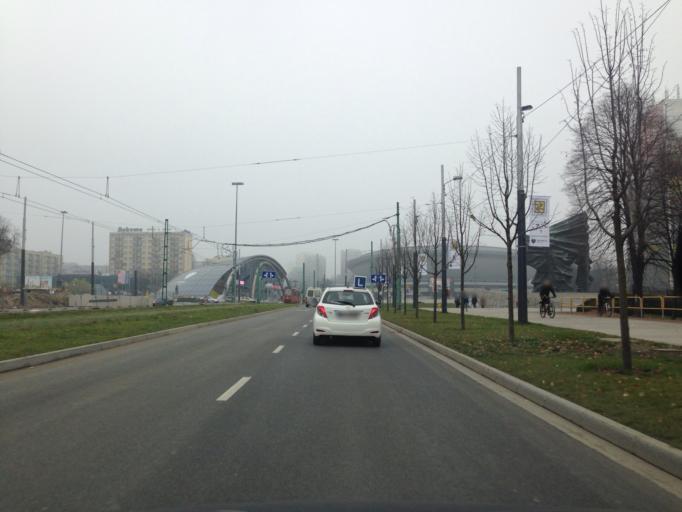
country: PL
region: Silesian Voivodeship
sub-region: Katowice
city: Katowice
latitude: 50.2627
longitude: 19.0231
